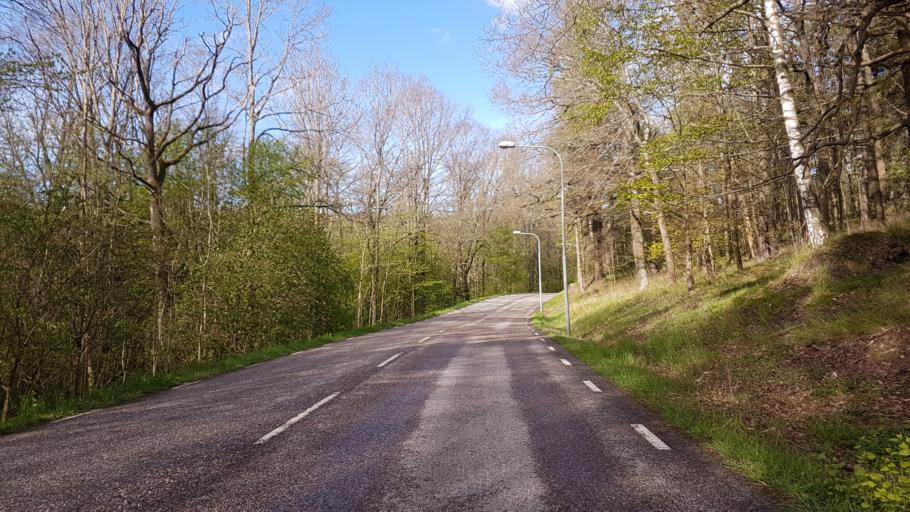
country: SE
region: Stockholm
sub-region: Stockholms Kommun
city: OEstermalm
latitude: 59.3562
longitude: 18.0745
